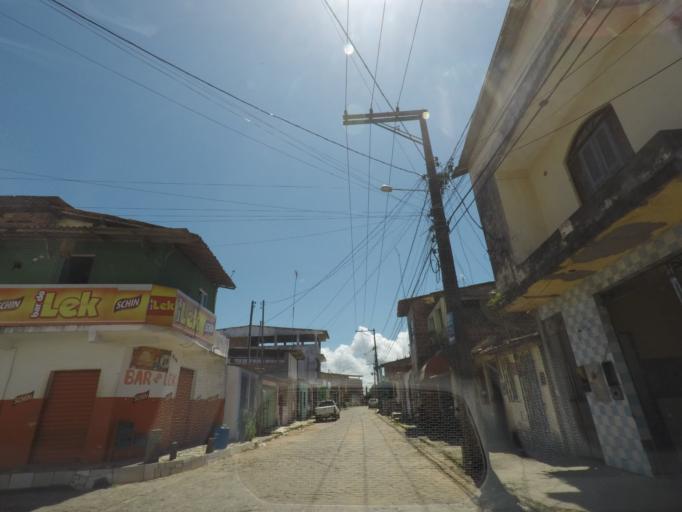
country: BR
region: Bahia
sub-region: Valenca
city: Valenca
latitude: -13.3551
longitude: -39.0628
